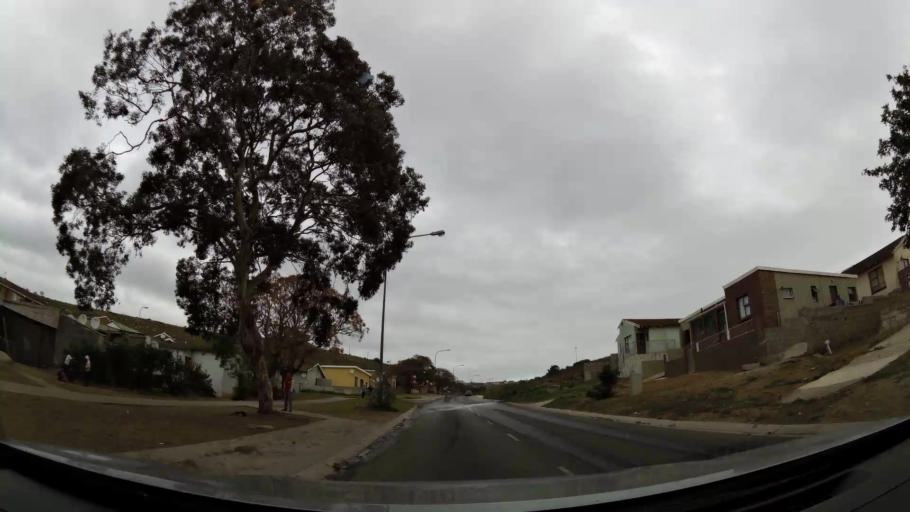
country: ZA
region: Eastern Cape
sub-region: Nelson Mandela Bay Metropolitan Municipality
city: Port Elizabeth
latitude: -33.9118
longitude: 25.5436
